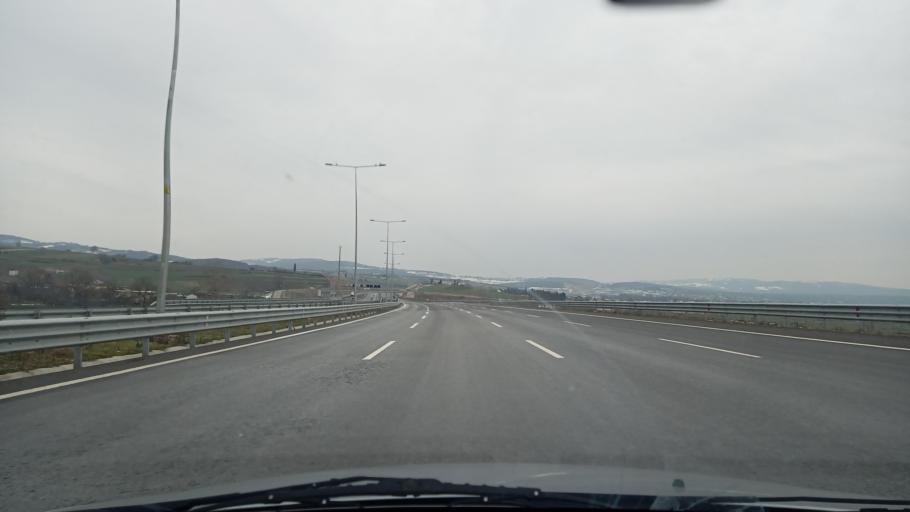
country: TR
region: Kocaeli
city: Kosekoy
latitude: 40.7918
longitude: 30.0391
